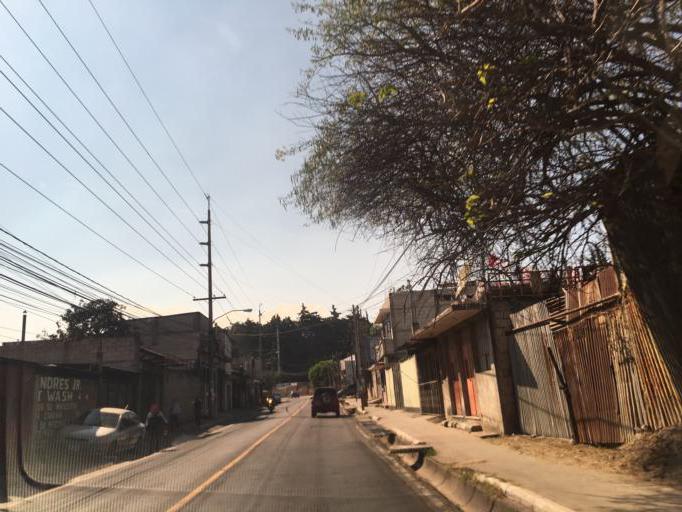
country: GT
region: Guatemala
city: Mixco
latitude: 14.6359
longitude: -90.5889
